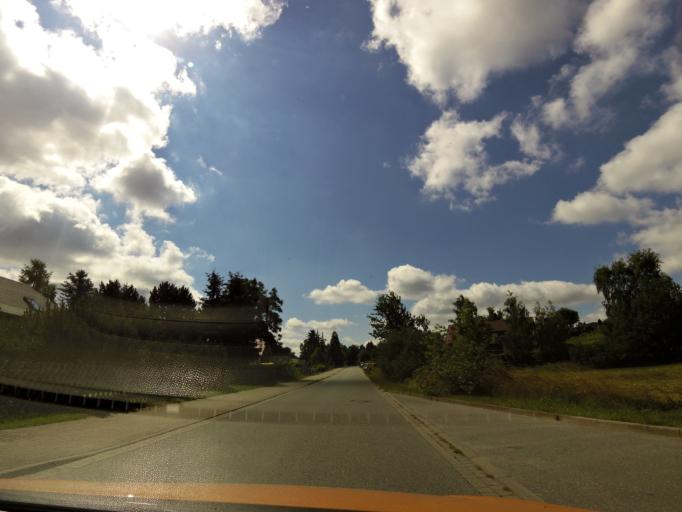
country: DE
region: Mecklenburg-Vorpommern
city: Plau am See
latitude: 53.4435
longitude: 12.2834
